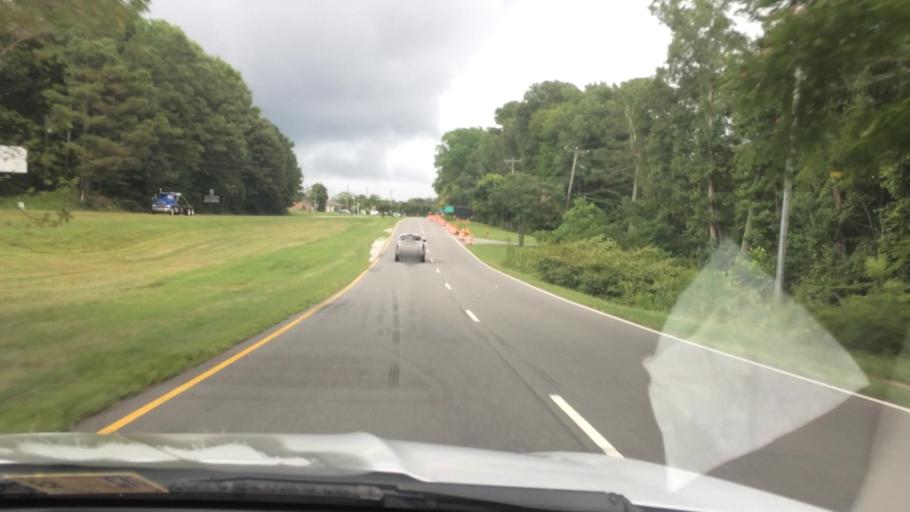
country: US
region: Virginia
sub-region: King William County
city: West Point
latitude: 37.4022
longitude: -76.8136
